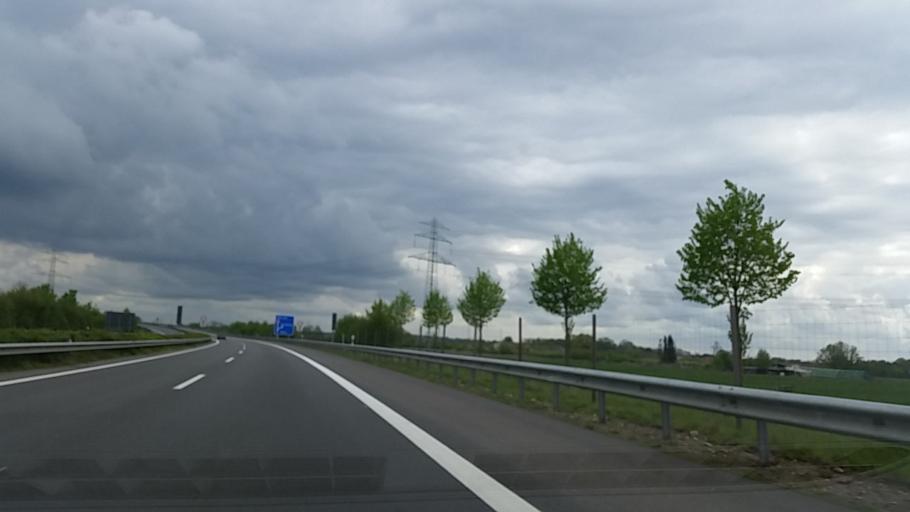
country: DE
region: Lower Saxony
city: Neuenkirchen
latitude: 53.5201
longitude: 9.5854
